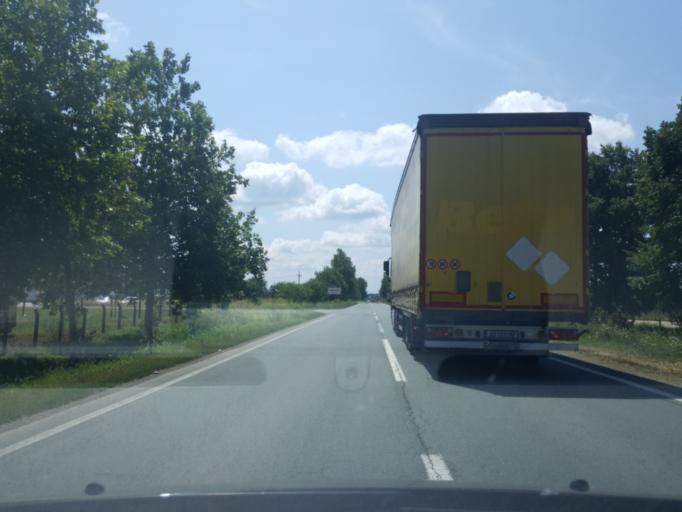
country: RS
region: Autonomna Pokrajina Vojvodina
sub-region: Sremski Okrug
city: Sremska Mitrovica
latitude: 44.9808
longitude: 19.6389
